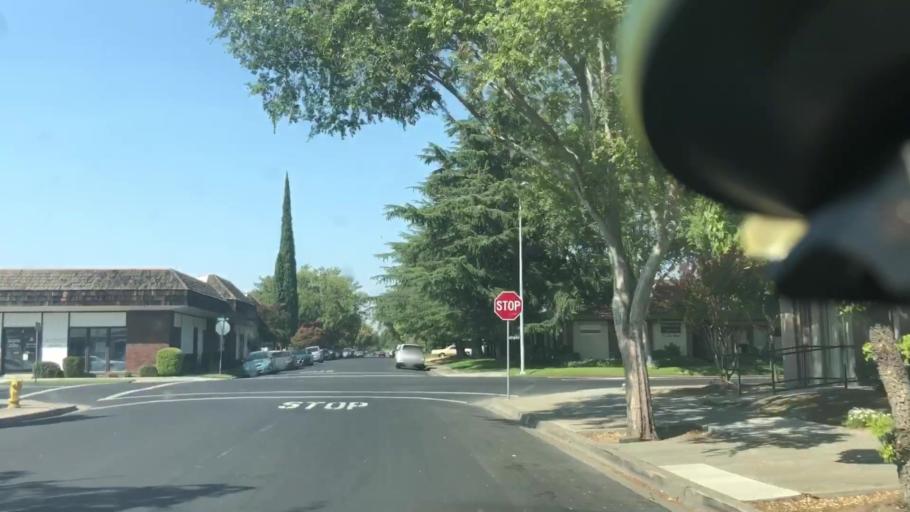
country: US
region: California
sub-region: San Joaquin County
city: Manteca
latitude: 37.7988
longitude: -121.2152
